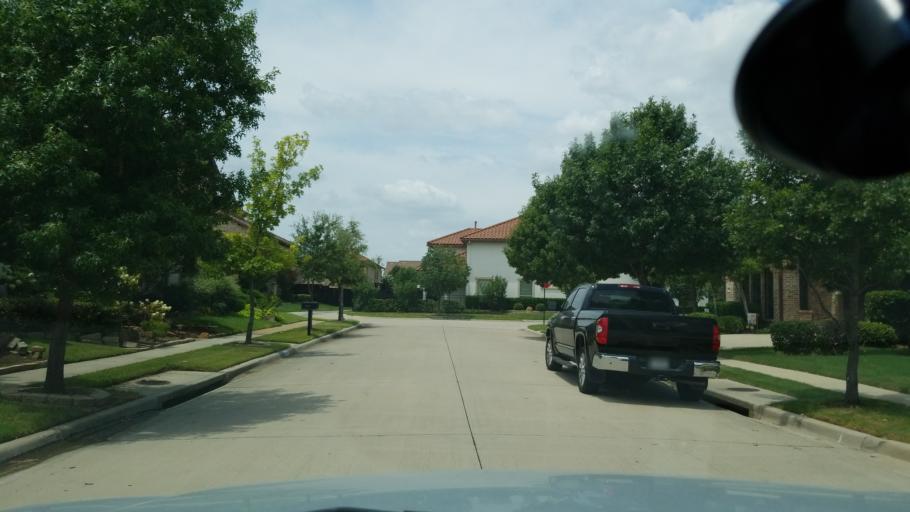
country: US
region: Texas
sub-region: Dallas County
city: Farmers Branch
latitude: 32.9054
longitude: -96.9345
